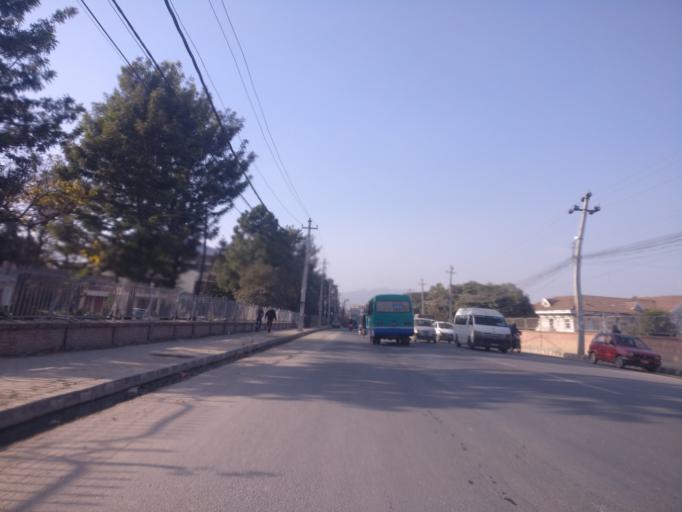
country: NP
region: Central Region
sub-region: Bagmati Zone
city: Patan
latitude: 27.6558
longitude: 85.3272
